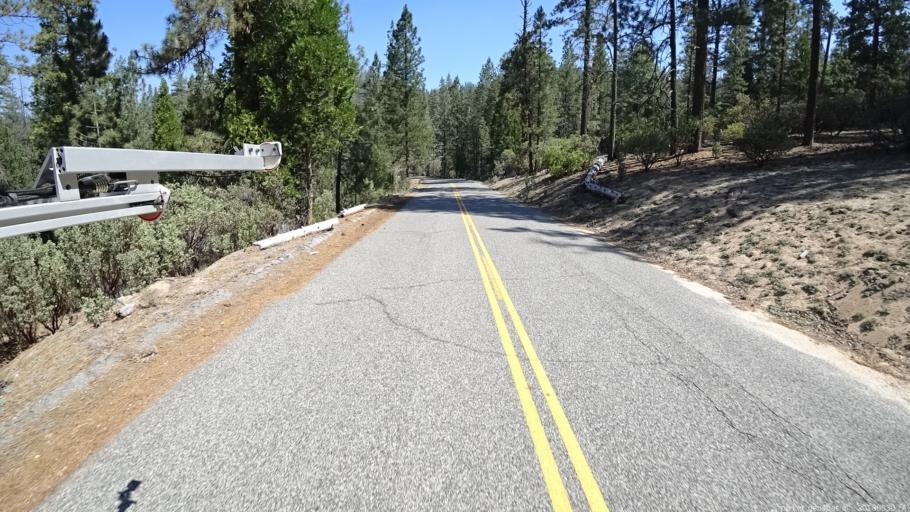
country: US
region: California
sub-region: Madera County
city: Oakhurst
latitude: 37.3799
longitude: -119.3809
